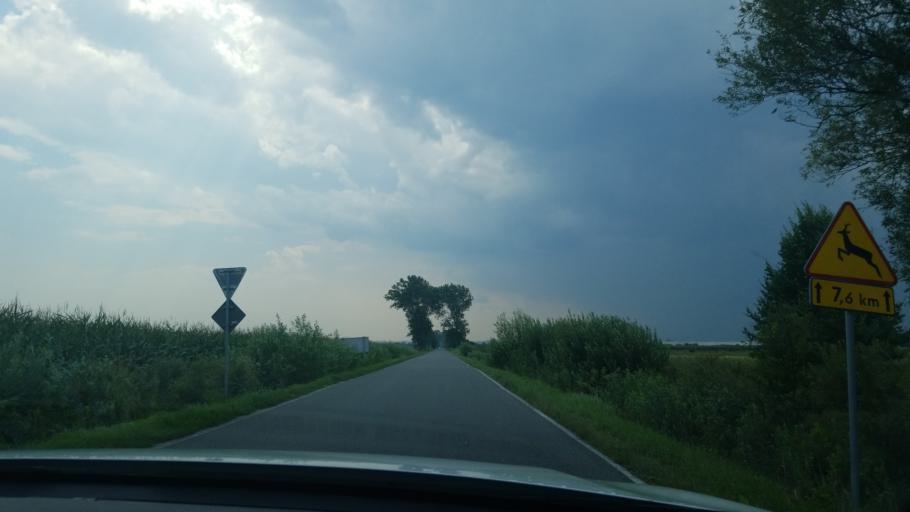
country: PL
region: Lesser Poland Voivodeship
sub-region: Powiat bochenski
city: Dziewin
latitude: 50.0912
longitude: 20.5112
